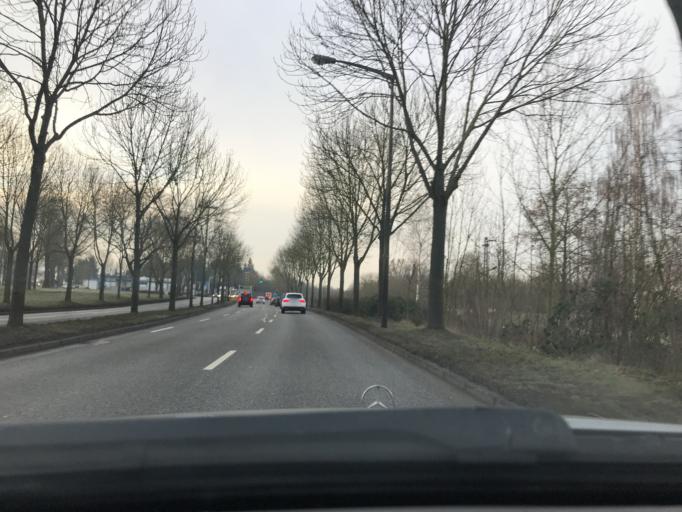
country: DE
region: Hesse
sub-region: Regierungsbezirk Kassel
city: Kassel
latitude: 51.2971
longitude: 9.5120
